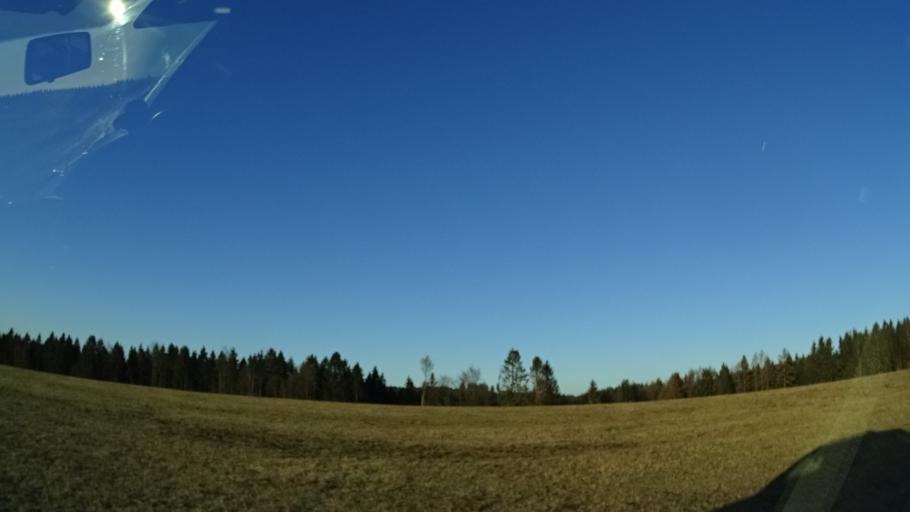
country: DE
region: Thuringia
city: Judenbach
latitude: 50.4108
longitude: 11.2290
